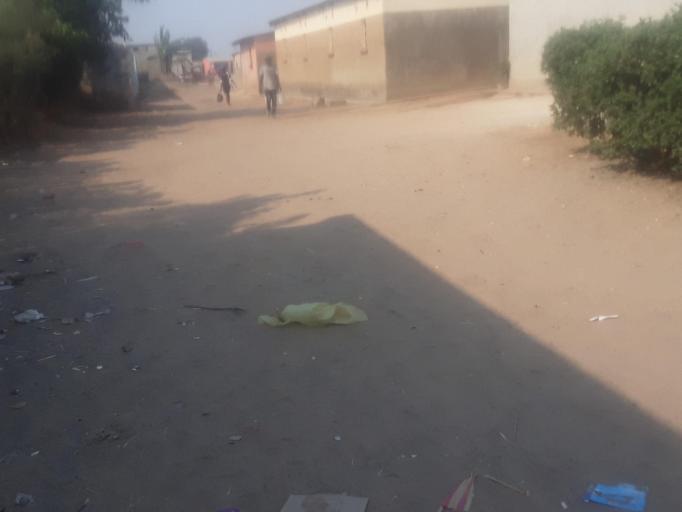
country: ZM
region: Lusaka
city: Lusaka
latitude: -15.3576
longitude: 28.2888
